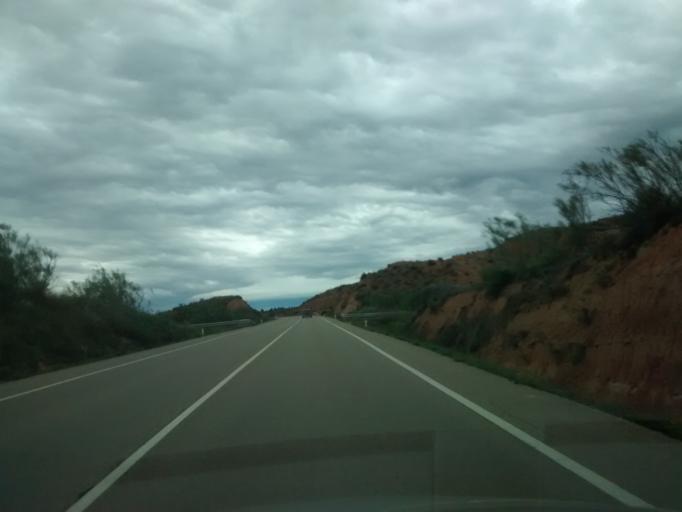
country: ES
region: Aragon
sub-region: Provincia de Zaragoza
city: Caspe
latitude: 41.2027
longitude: 0.0407
